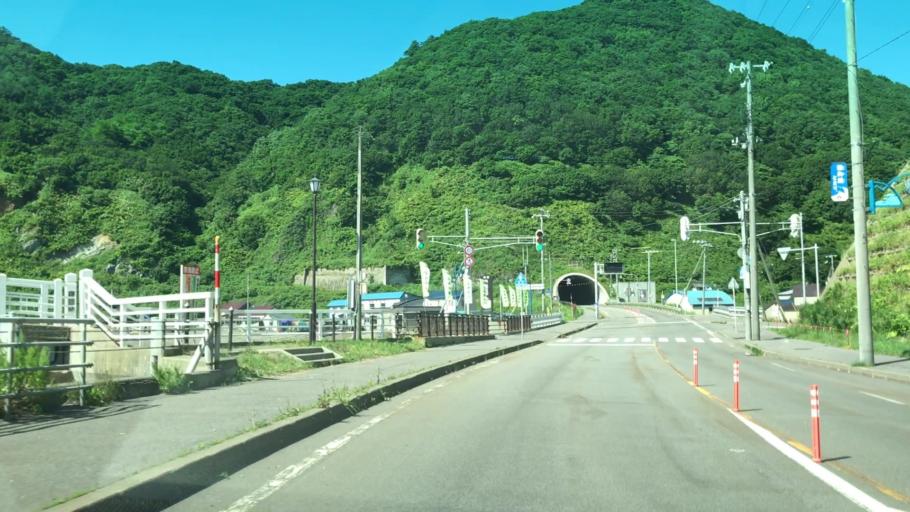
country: JP
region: Hokkaido
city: Iwanai
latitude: 43.1119
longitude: 140.4504
